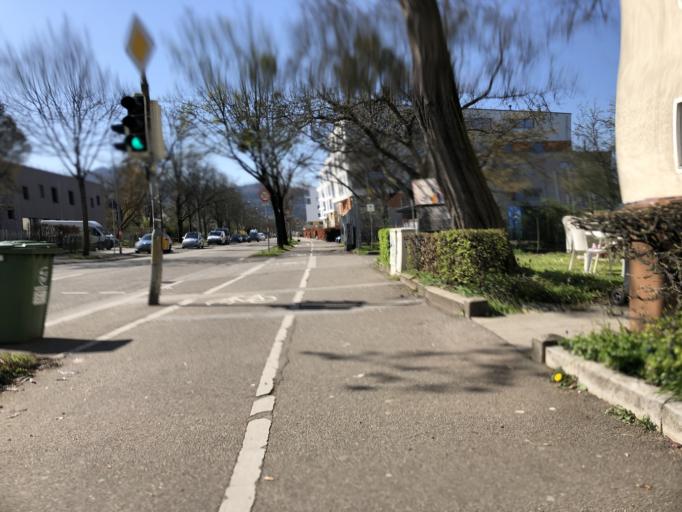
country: DE
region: Baden-Wuerttemberg
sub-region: Freiburg Region
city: Merzhausen
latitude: 47.9887
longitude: 7.8134
